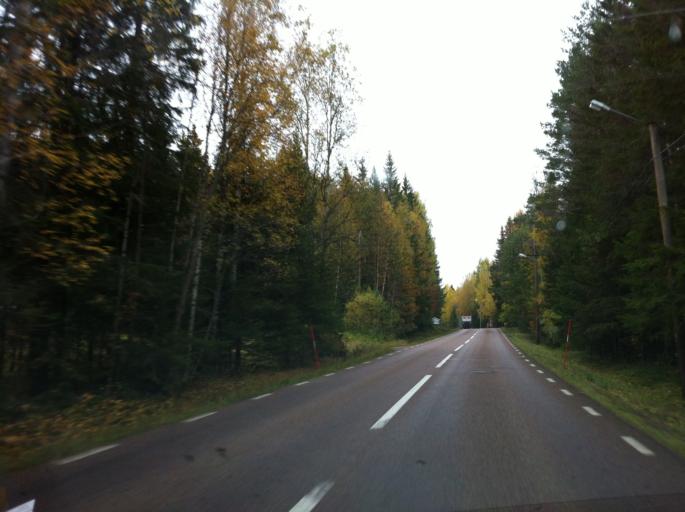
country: SE
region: Dalarna
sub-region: Ludvika Kommun
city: Grangesberg
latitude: 60.1587
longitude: 14.9729
